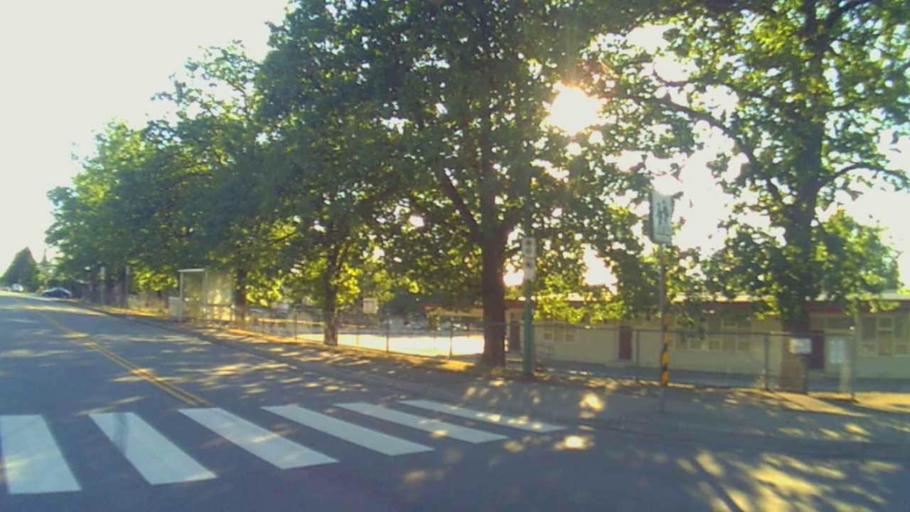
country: CA
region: British Columbia
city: New Westminster
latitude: 49.2334
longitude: -122.9085
